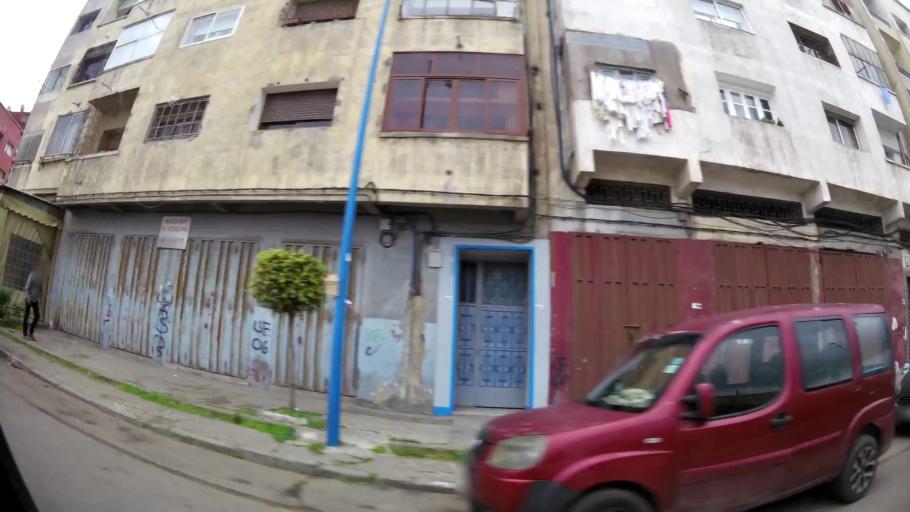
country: MA
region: Grand Casablanca
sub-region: Casablanca
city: Casablanca
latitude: 33.5954
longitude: -7.5582
